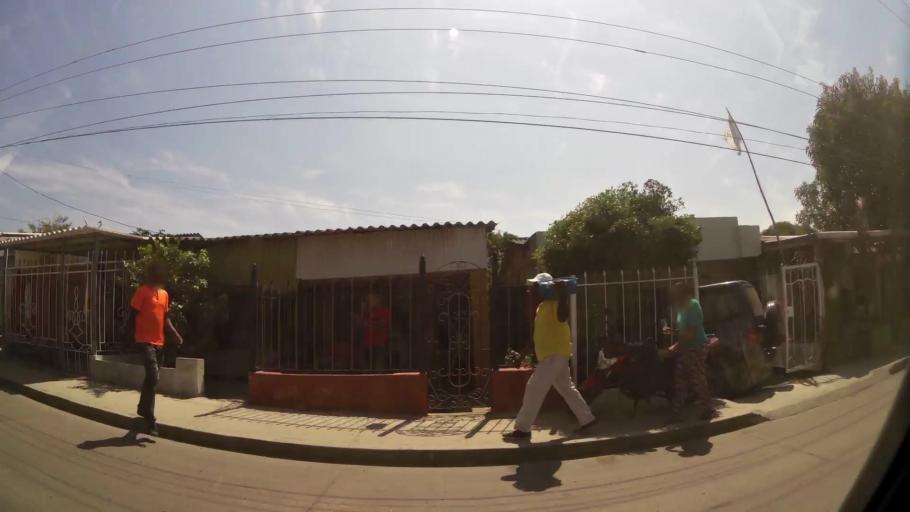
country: CO
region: Atlantico
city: Barranquilla
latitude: 10.9640
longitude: -74.8156
